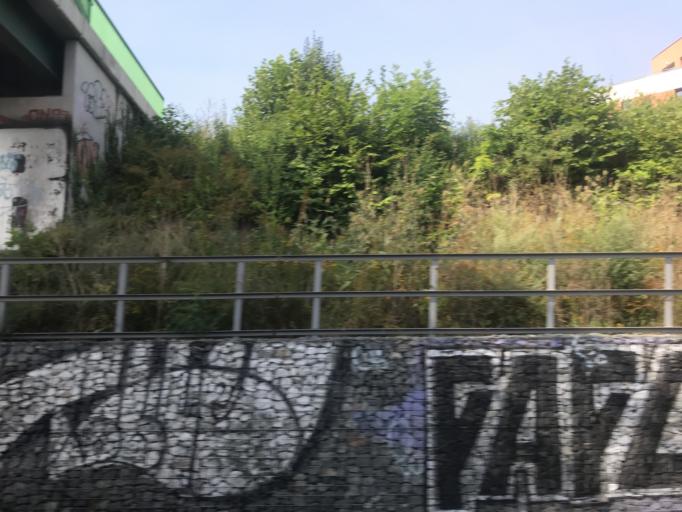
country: CZ
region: Praha
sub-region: Praha 14
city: Hostavice
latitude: 50.0577
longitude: 14.5228
